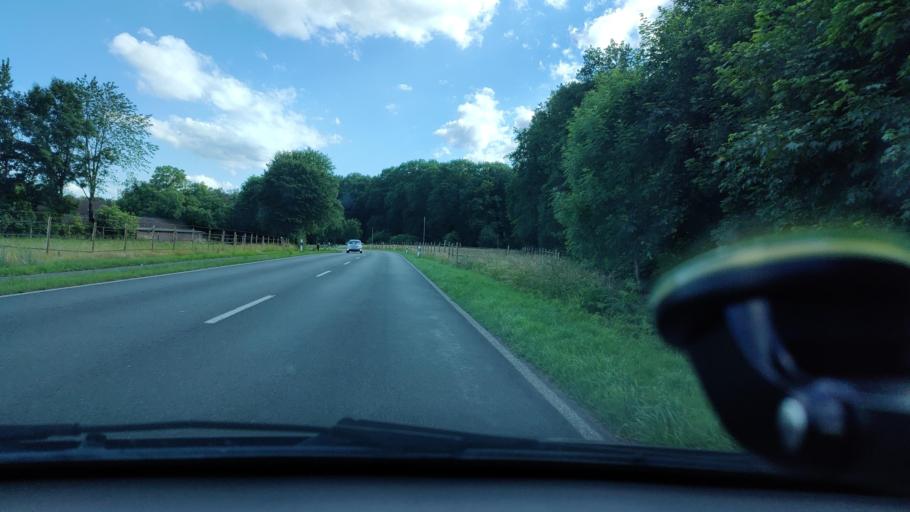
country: DE
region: North Rhine-Westphalia
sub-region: Regierungsbezirk Dusseldorf
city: Alpen
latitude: 51.5631
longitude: 6.5280
